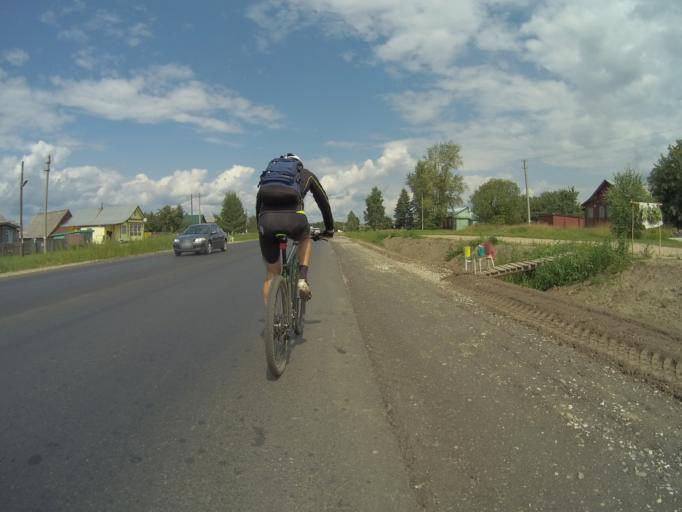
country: RU
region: Vladimir
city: Kideksha
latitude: 56.5160
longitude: 40.5523
